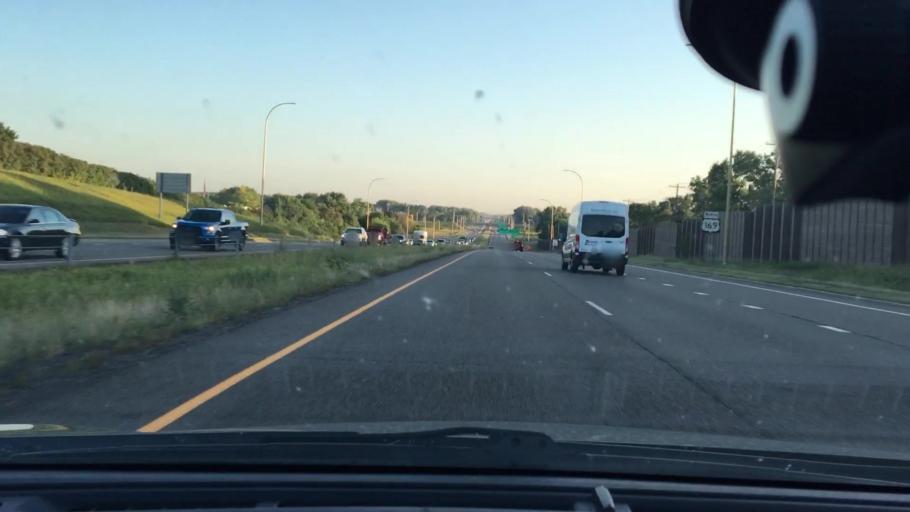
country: US
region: Minnesota
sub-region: Hennepin County
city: New Hope
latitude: 45.0256
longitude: -93.3997
